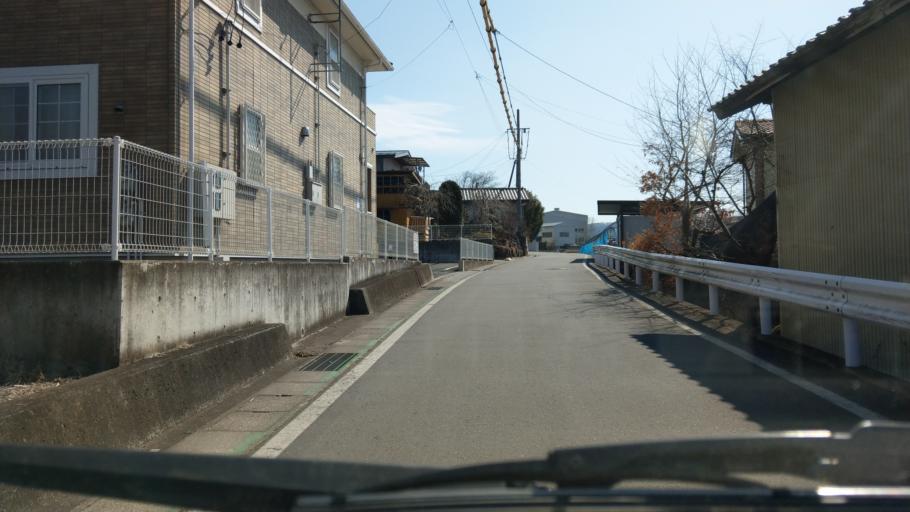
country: JP
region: Nagano
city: Komoro
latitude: 36.3459
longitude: 138.3862
